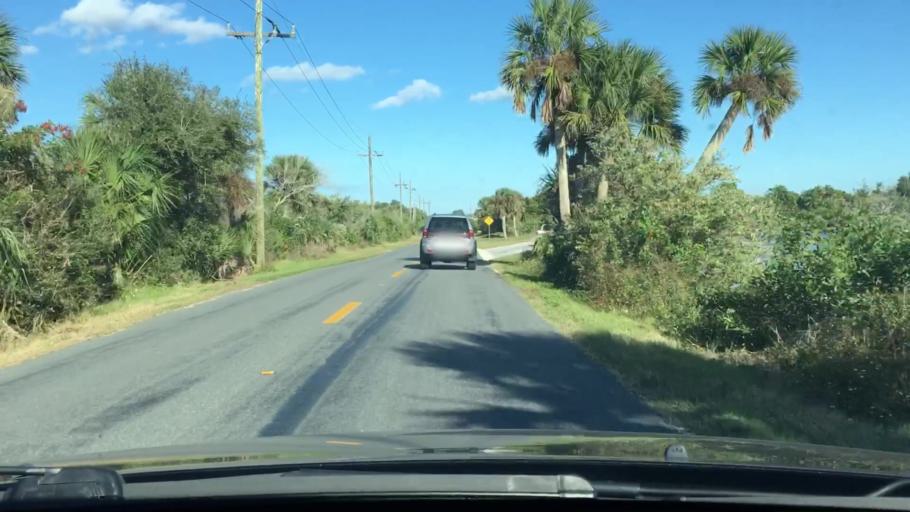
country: US
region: Florida
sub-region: Volusia County
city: Ormond-by-the-Sea
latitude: 29.4064
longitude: -81.1052
